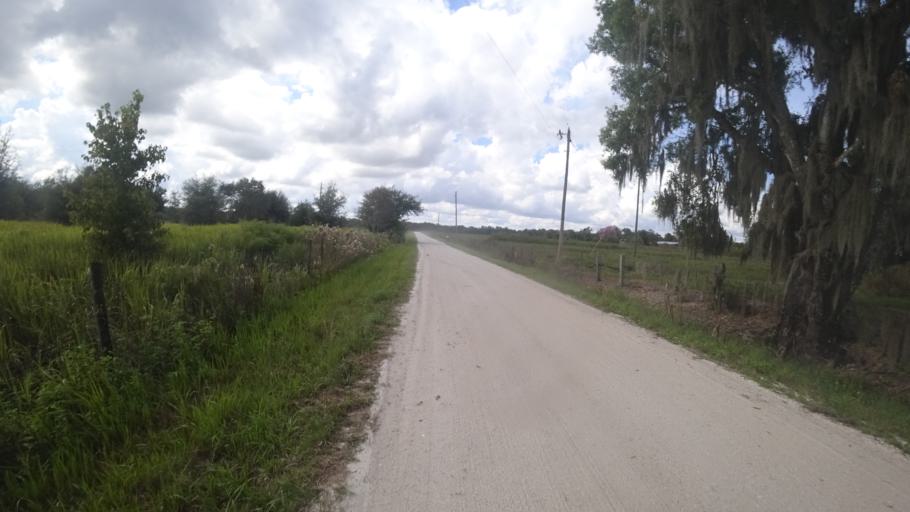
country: US
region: Florida
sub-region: Hillsborough County
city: Wimauma
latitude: 27.5914
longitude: -82.1836
